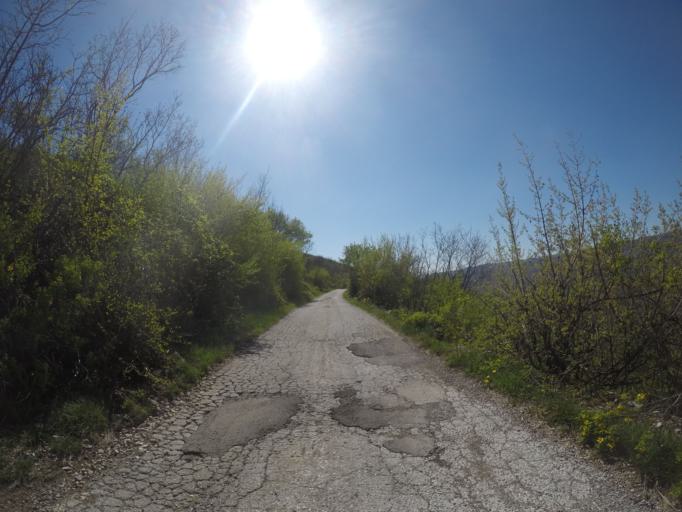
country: ME
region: Danilovgrad
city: Danilovgrad
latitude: 42.5364
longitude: 19.0149
